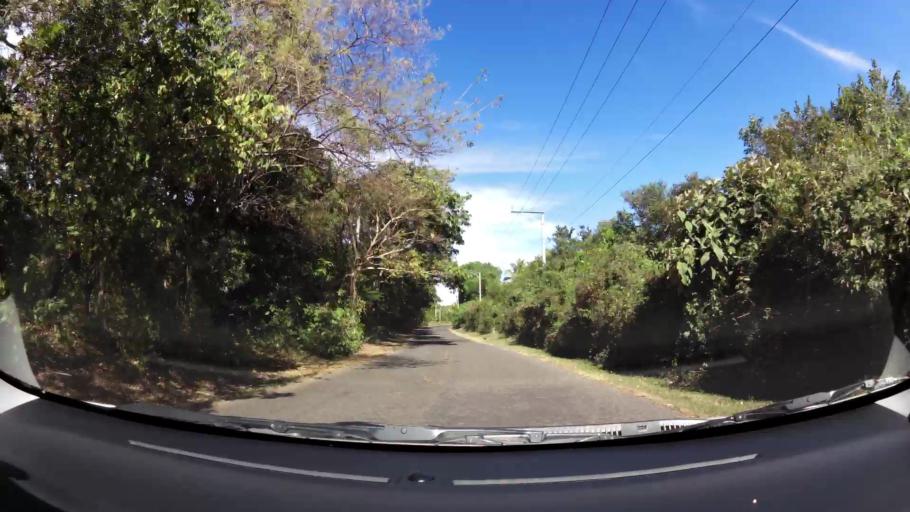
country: SV
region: Cuscatlan
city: Suchitoto
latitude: 13.9302
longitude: -89.0431
